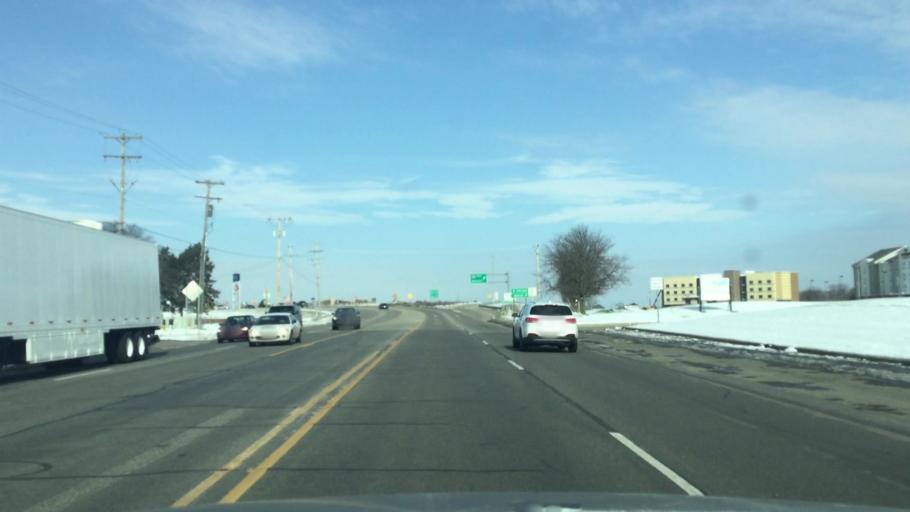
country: US
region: Michigan
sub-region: Kalamazoo County
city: Eastwood
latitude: 42.2551
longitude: -85.5308
